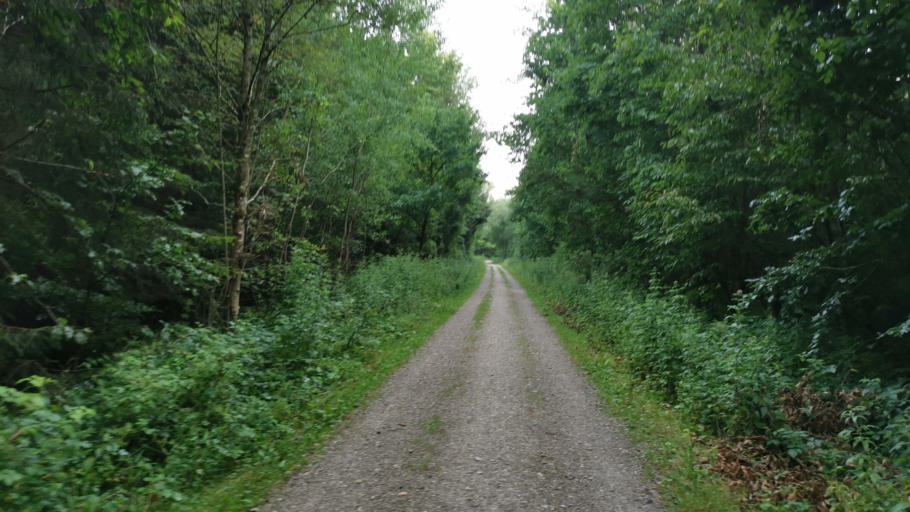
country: DE
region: Bavaria
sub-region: Upper Bavaria
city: Pullach im Isartal
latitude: 48.0520
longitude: 11.5026
